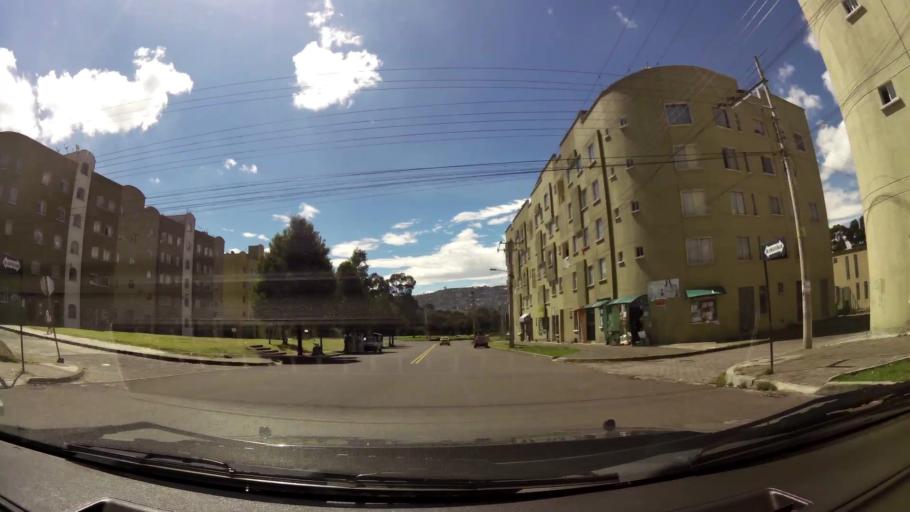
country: EC
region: Pichincha
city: Quito
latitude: -0.2898
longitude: -78.5515
